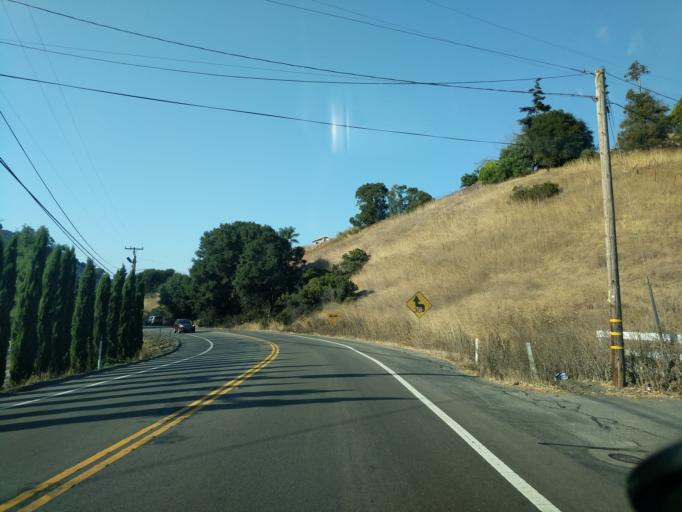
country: US
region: California
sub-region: Alameda County
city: Fairview
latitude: 37.7291
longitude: -122.0339
